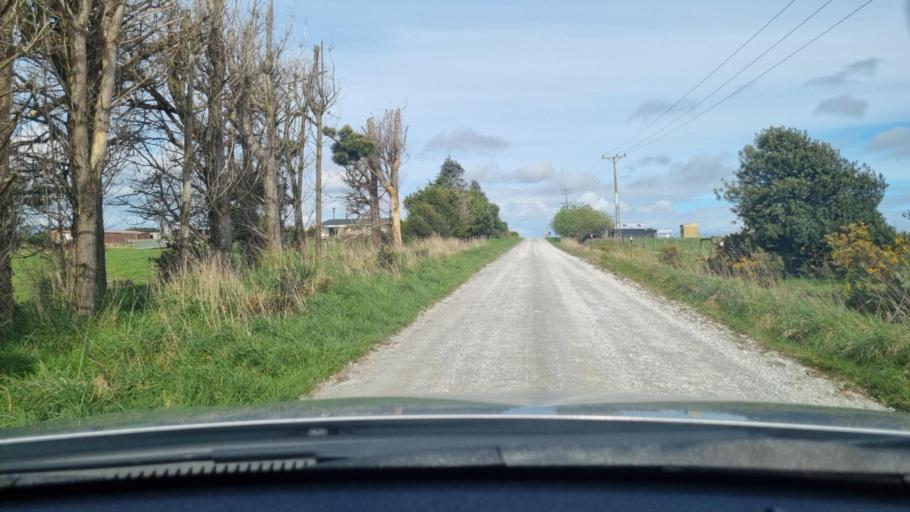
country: NZ
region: Southland
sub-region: Invercargill City
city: Invercargill
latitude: -46.4521
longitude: 168.3819
